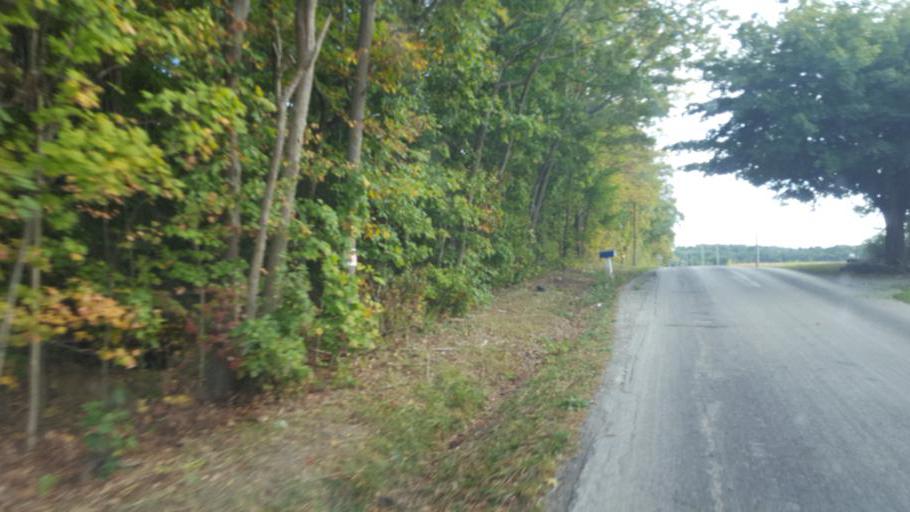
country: US
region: Ohio
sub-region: Richland County
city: Lexington
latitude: 40.5846
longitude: -82.6051
